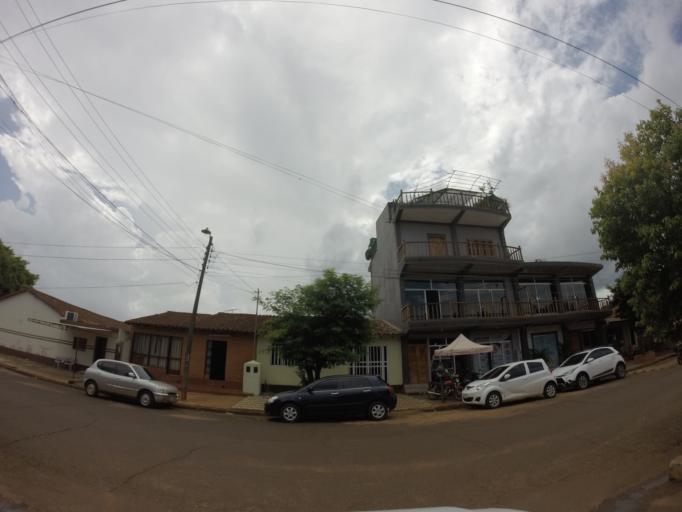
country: PY
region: Alto Parana
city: Ciudad del Este
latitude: -25.4145
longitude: -54.6285
